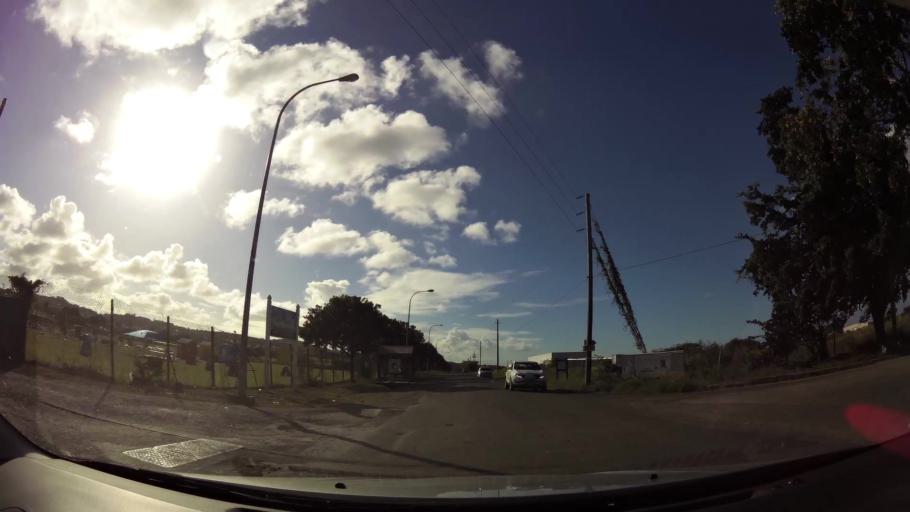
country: AG
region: Saint George
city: Piggotts
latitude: 17.1161
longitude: -61.8078
